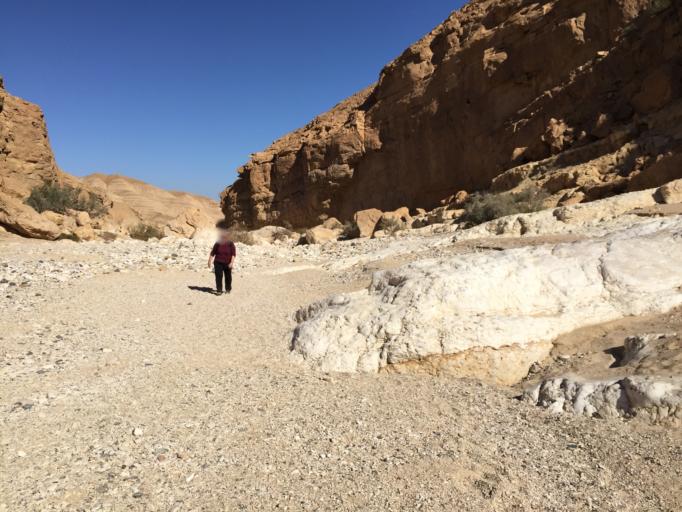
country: IL
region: Southern District
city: Mitzpe Ramon
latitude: 30.5993
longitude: 34.9469
